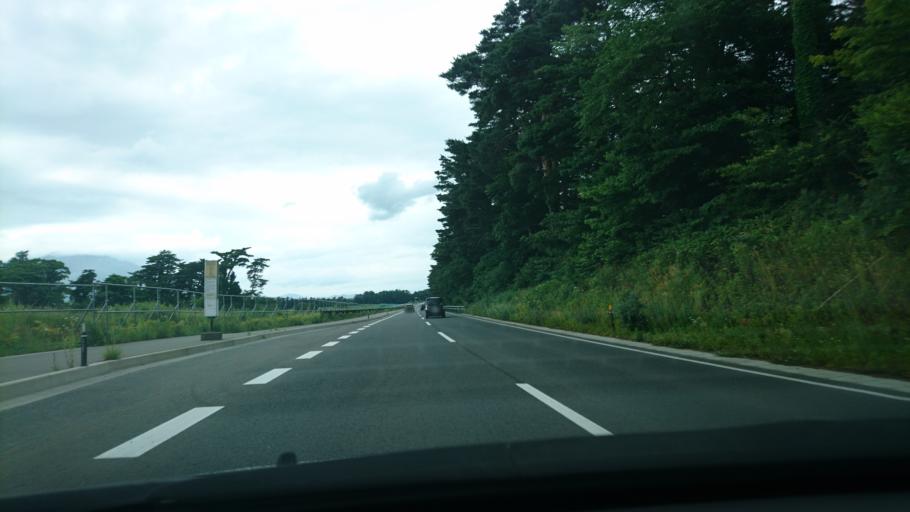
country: JP
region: Iwate
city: Morioka-shi
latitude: 39.7597
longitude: 141.1336
